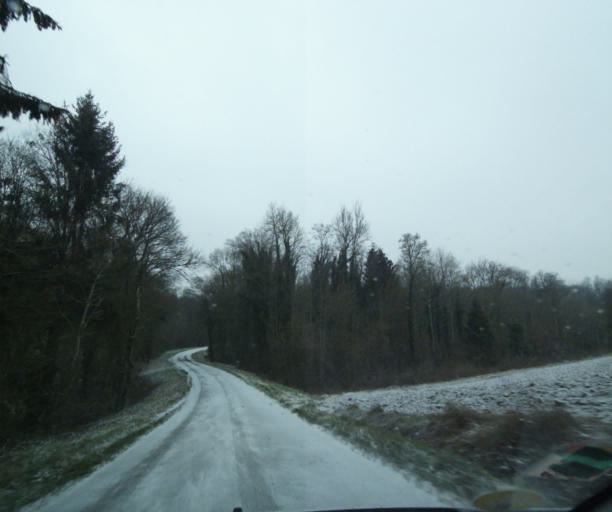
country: FR
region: Champagne-Ardenne
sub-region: Departement de la Haute-Marne
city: Bienville
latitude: 48.4833
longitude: 5.0475
